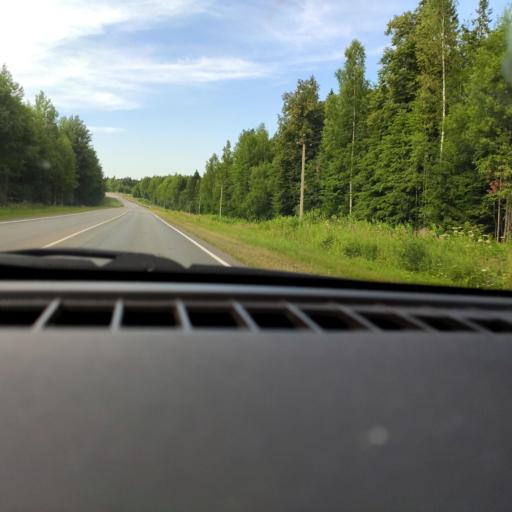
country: RU
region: Perm
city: Polazna
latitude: 58.3102
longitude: 56.1523
